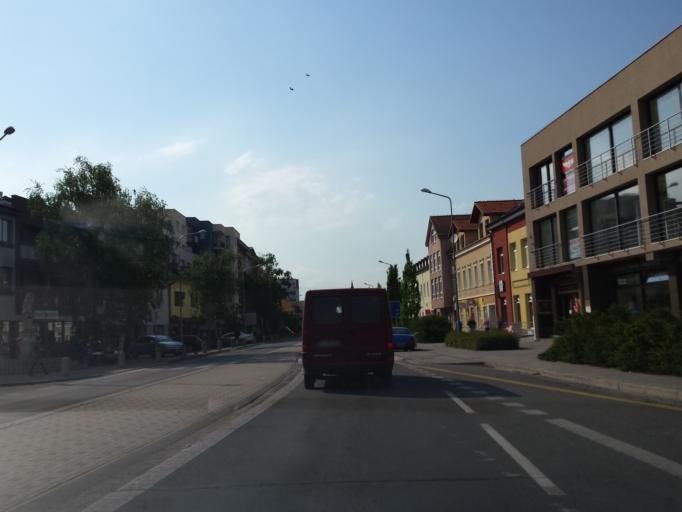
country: SK
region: Bratislavsky
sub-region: Okres Malacky
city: Malacky
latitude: 48.4378
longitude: 17.0173
